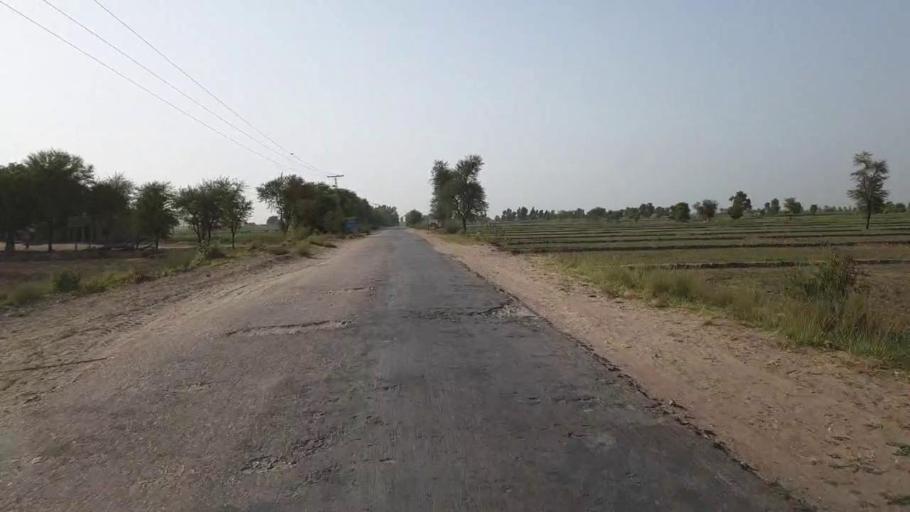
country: PK
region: Sindh
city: Jam Sahib
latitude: 26.3860
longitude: 68.8834
